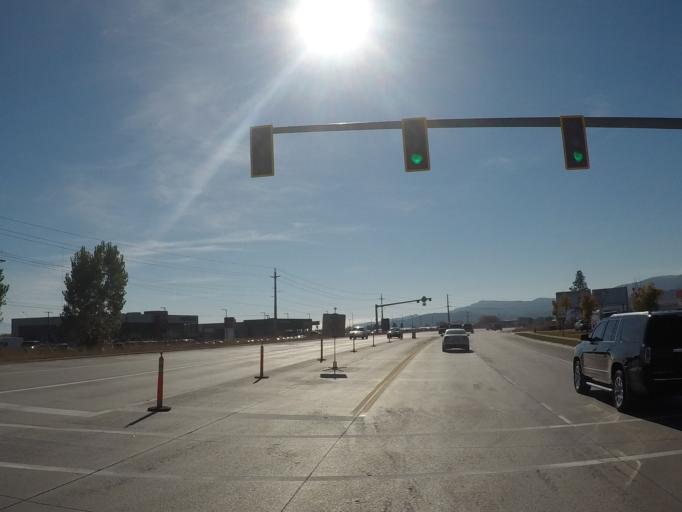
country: US
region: Montana
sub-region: Flathead County
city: Kalispell
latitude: 48.1646
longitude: -114.2884
